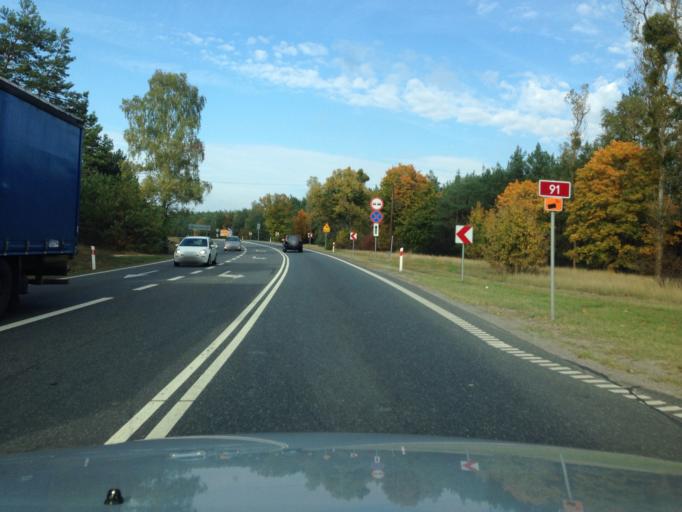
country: PL
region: Kujawsko-Pomorskie
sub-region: Grudziadz
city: Grudziadz
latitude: 53.5210
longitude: 18.6892
